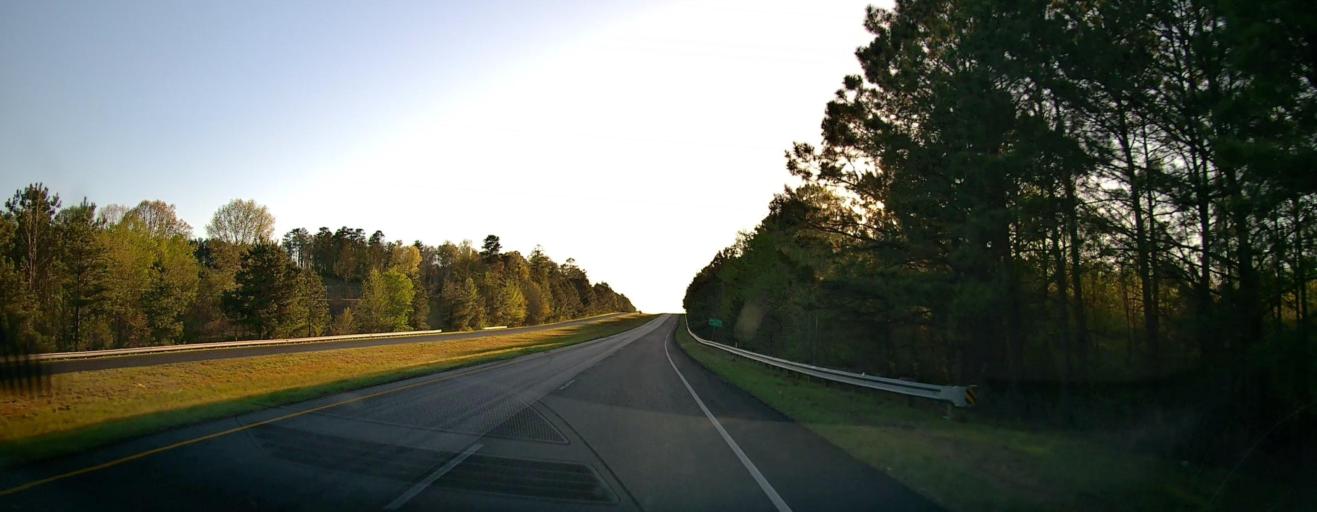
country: US
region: Georgia
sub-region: Wilkinson County
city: Gordon
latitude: 32.8564
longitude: -83.3868
